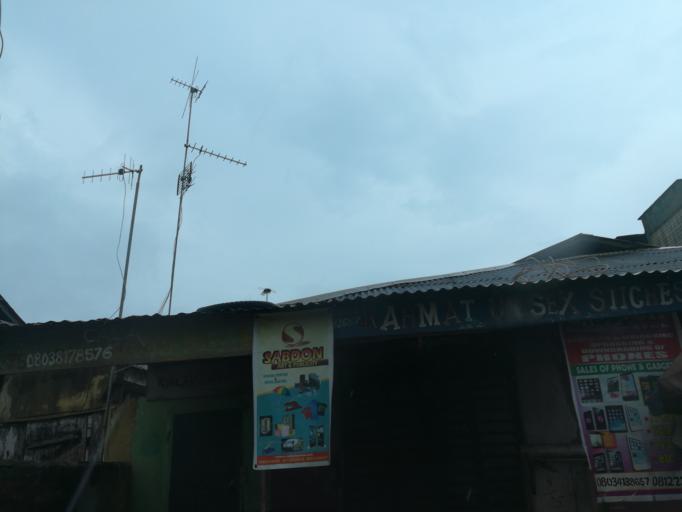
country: NG
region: Lagos
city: Oshodi
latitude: 6.5743
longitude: 3.3429
